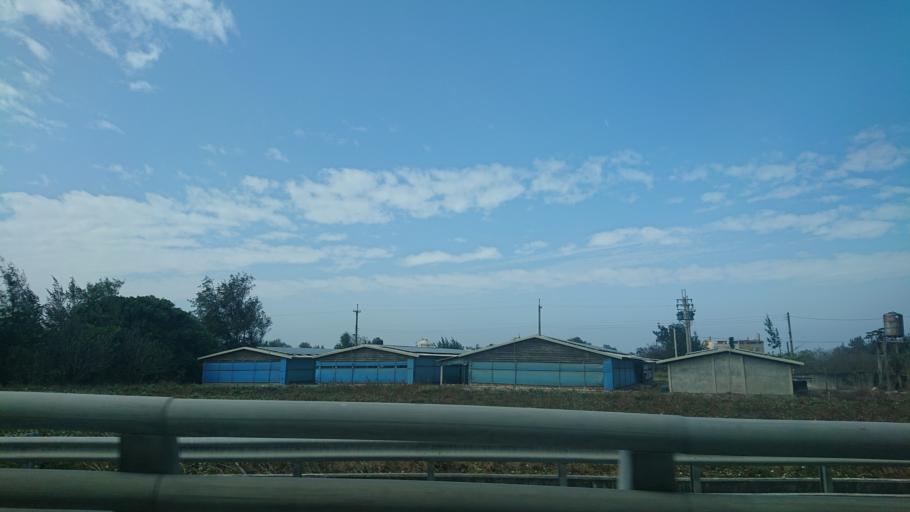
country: TW
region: Taiwan
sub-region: Yunlin
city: Douliu
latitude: 23.8602
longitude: 120.2956
